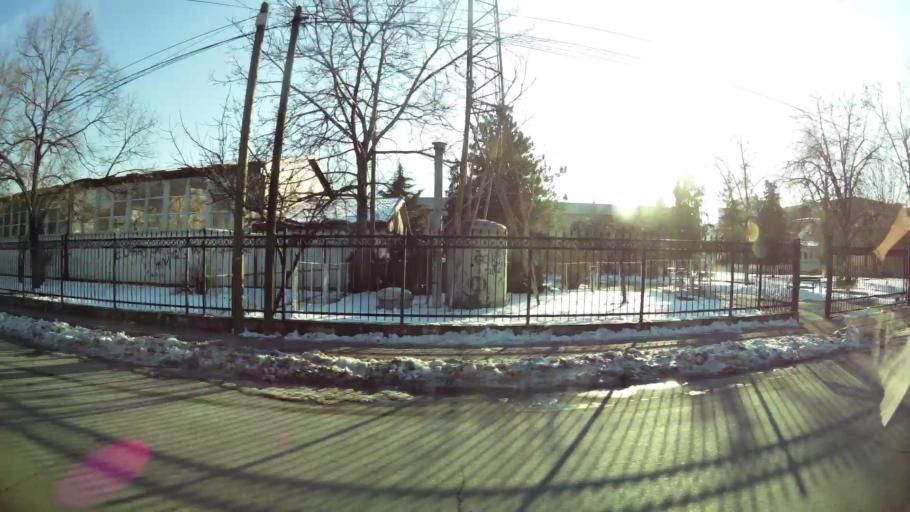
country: MK
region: Karpos
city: Skopje
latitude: 42.0013
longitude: 21.3939
